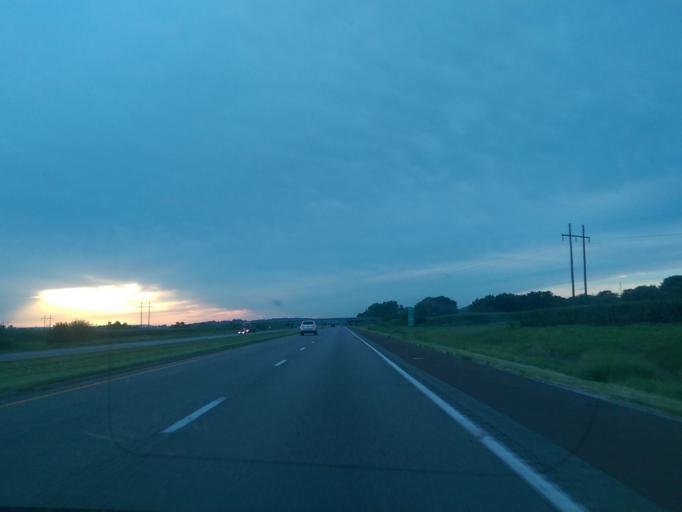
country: US
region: Missouri
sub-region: Holt County
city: Mound City
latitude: 40.1764
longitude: -95.3078
